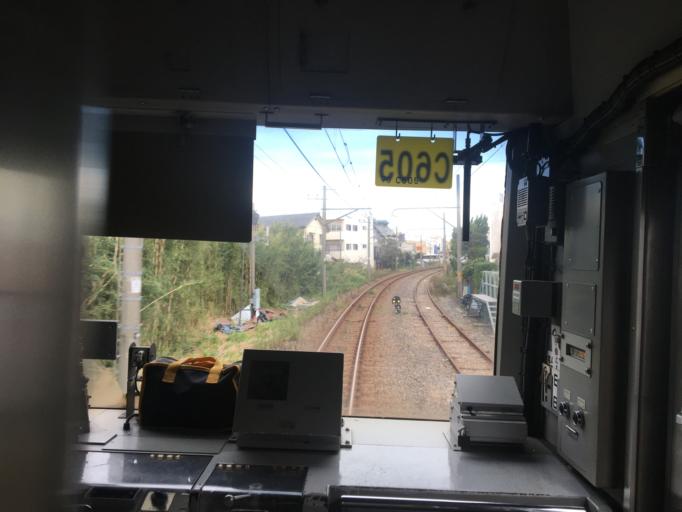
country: JP
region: Chiba
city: Tateyama
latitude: 34.9910
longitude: 139.8624
